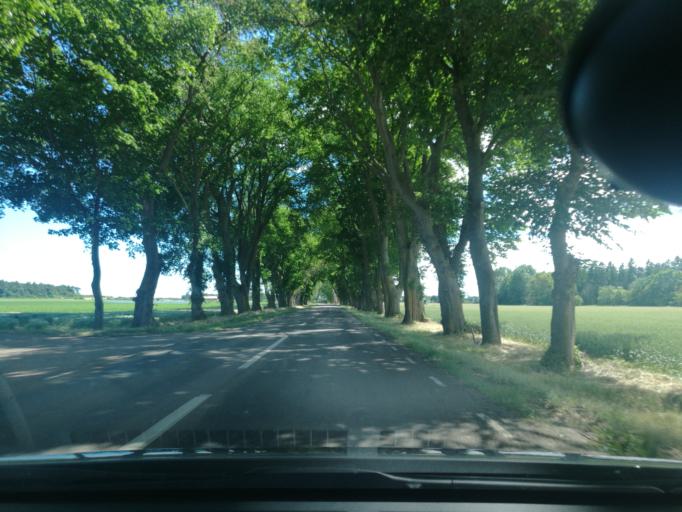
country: SE
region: Kalmar
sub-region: Morbylanga Kommun
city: Moerbylanga
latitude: 56.3381
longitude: 16.4109
